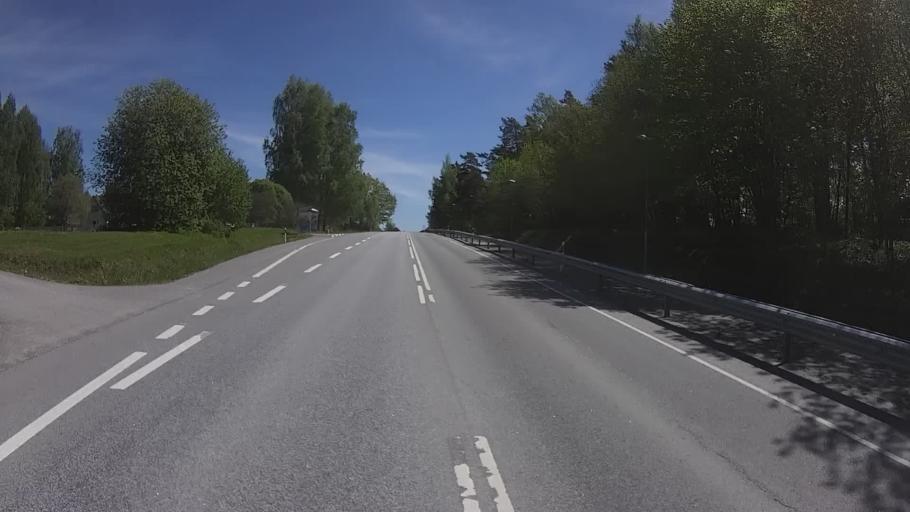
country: EE
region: Vorumaa
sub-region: Voru linn
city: Voru
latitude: 57.8124
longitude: 27.0495
